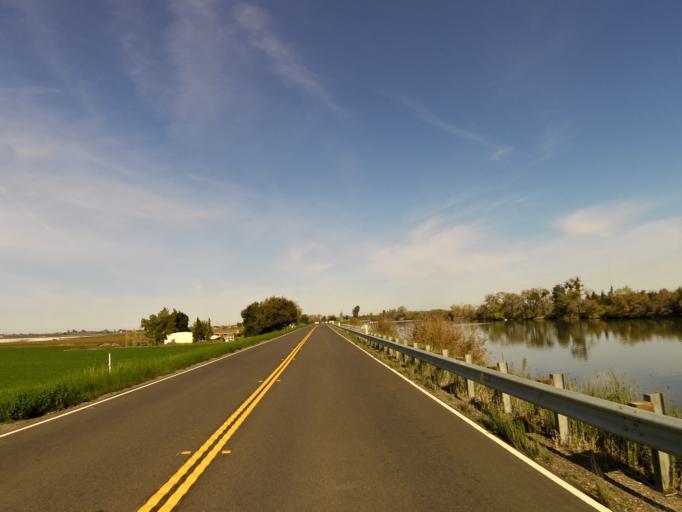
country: US
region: California
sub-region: Sacramento County
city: Walnut Grove
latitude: 38.2161
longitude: -121.5585
